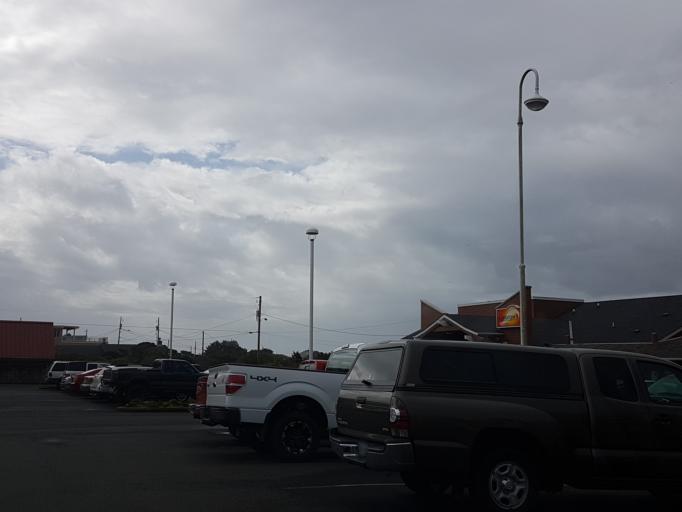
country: US
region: Oregon
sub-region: Lincoln County
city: Newport
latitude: 44.6296
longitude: -124.0640
